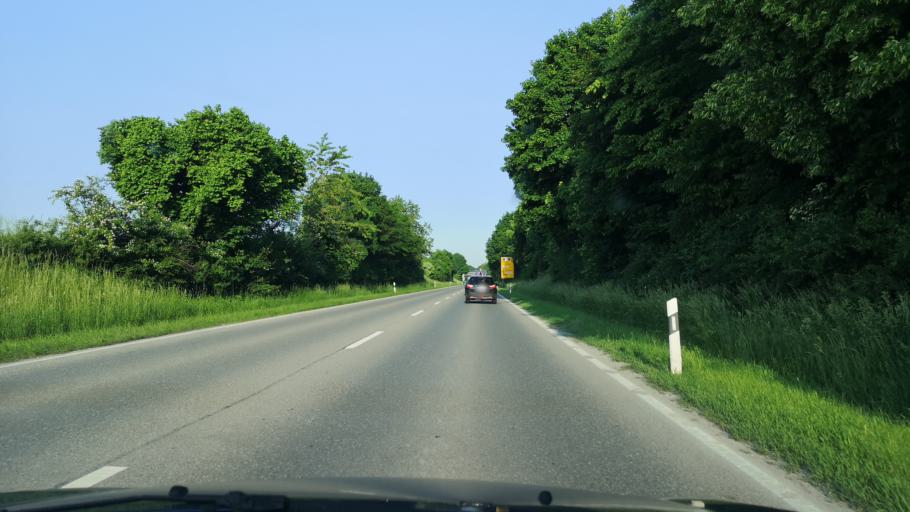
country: DE
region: Bavaria
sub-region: Upper Bavaria
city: Kirchheim bei Muenchen
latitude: 48.1729
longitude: 11.7603
